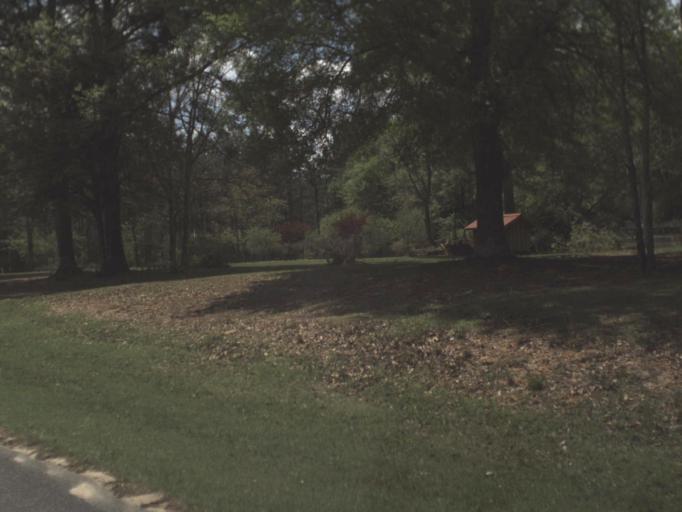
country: US
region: Florida
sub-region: Okaloosa County
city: Crestview
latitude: 30.9656
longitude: -86.6320
